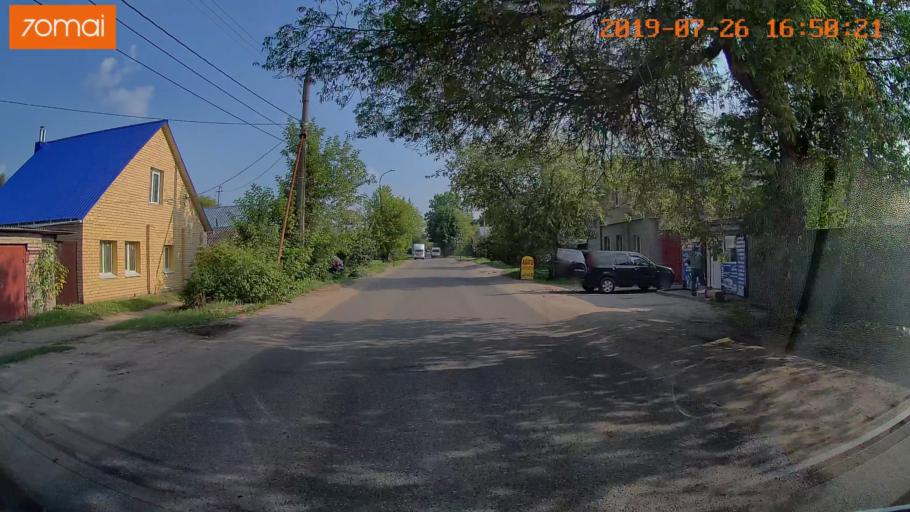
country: RU
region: Ivanovo
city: Bogorodskoye
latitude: 57.0246
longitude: 41.0207
